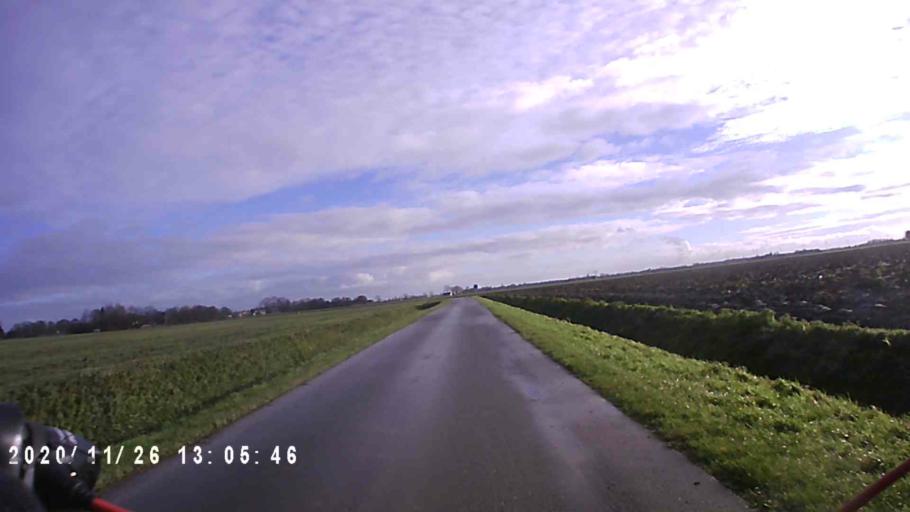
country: NL
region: Groningen
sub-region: Gemeente Appingedam
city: Appingedam
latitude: 53.3524
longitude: 6.8393
